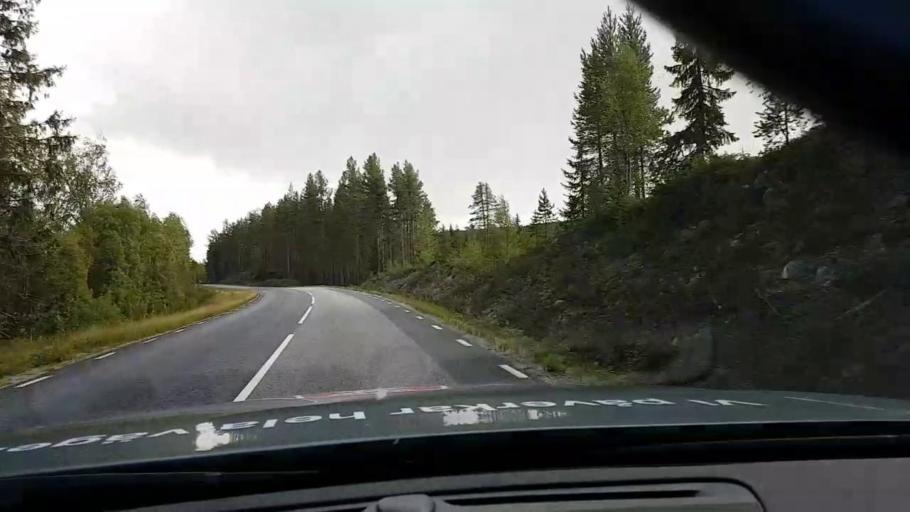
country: SE
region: Vaesterbotten
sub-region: Asele Kommun
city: Asele
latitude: 63.8432
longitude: 17.4237
